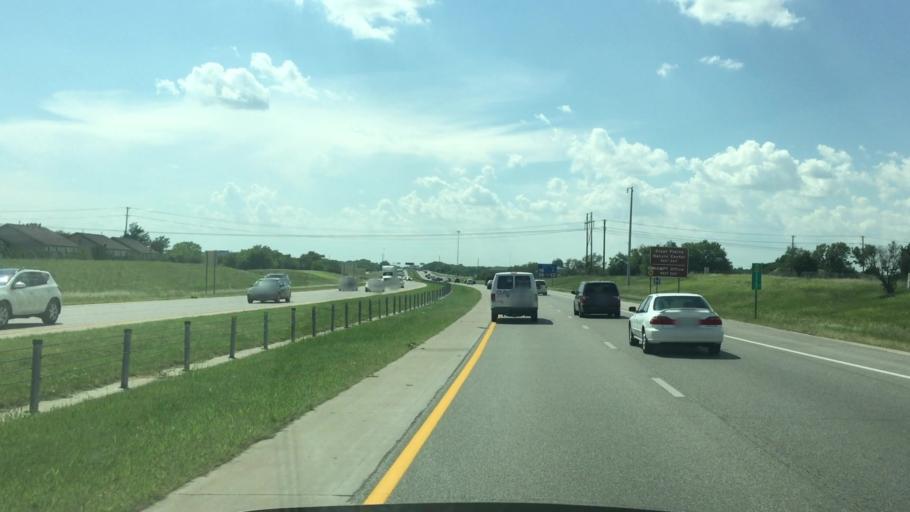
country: US
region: Kansas
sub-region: Sedgwick County
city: Bellaire
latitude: 37.7453
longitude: -97.2514
